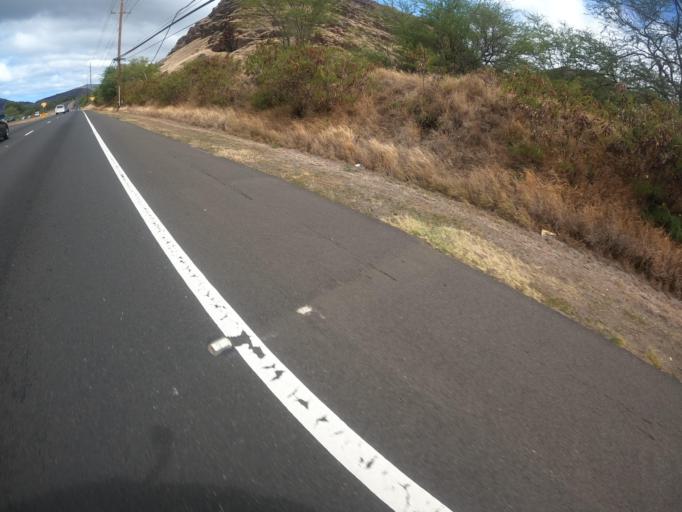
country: US
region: Hawaii
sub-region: Honolulu County
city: Nanakuli
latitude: 21.3626
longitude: -158.1323
